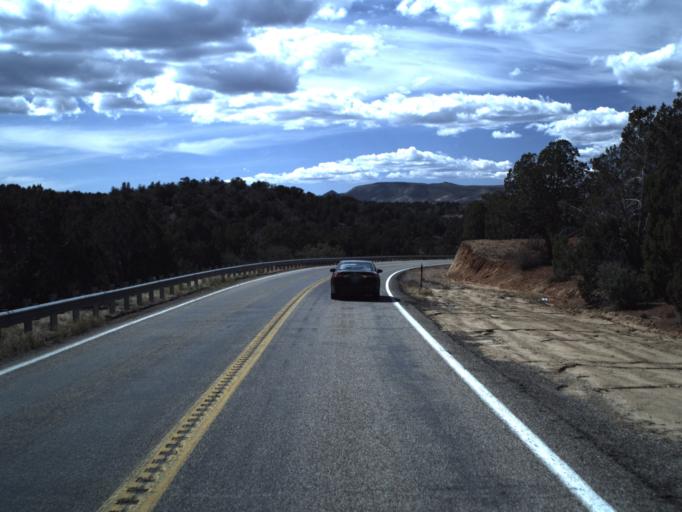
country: US
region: Utah
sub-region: Washington County
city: Enterprise
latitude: 37.5402
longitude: -113.6666
